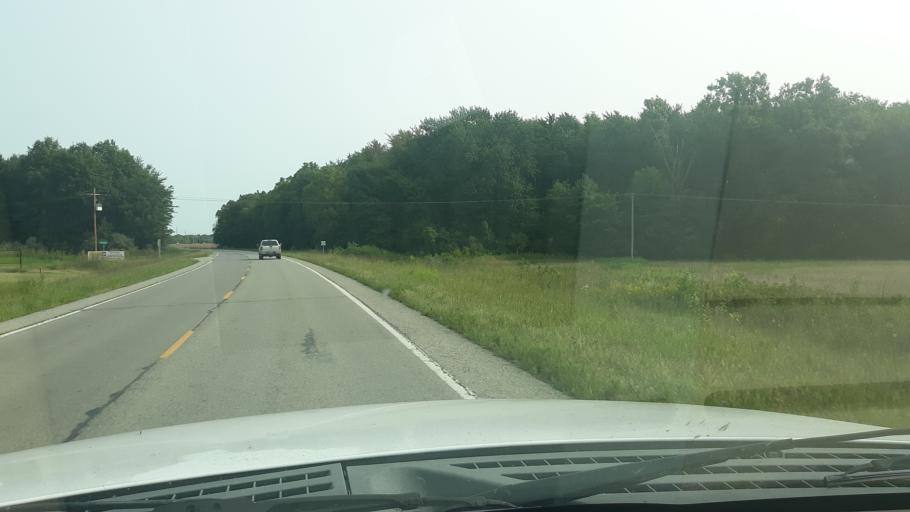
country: US
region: Illinois
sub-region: White County
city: Norris City
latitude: 37.9700
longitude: -88.3225
